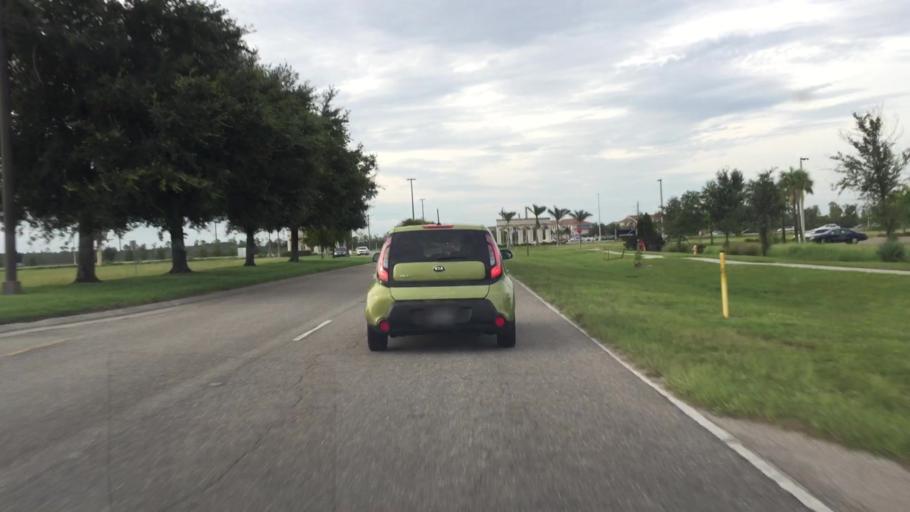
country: US
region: Florida
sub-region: Lee County
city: Fort Myers
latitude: 26.6297
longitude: -81.7930
